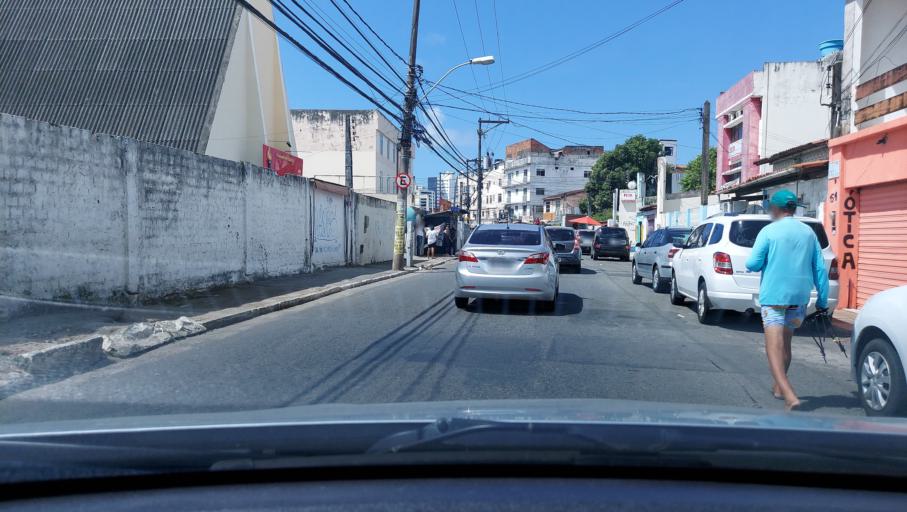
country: BR
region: Bahia
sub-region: Salvador
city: Salvador
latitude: -12.9869
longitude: -38.4786
